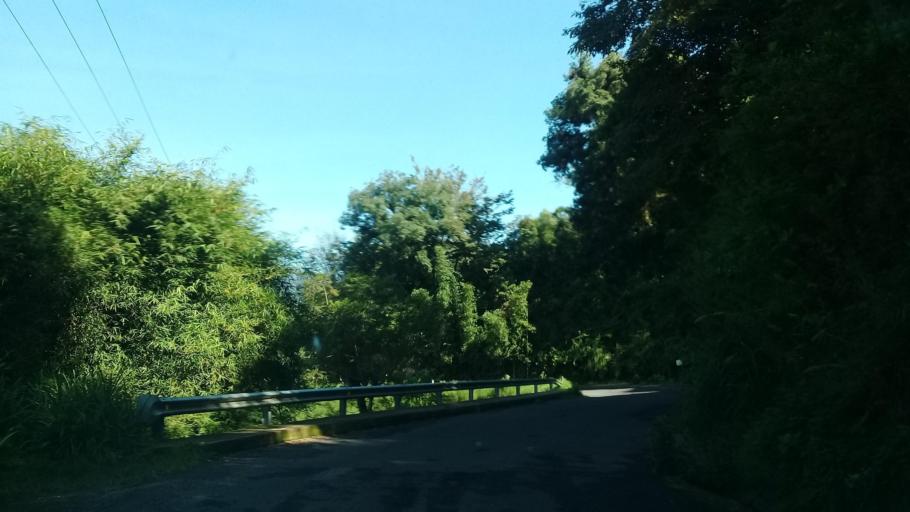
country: MX
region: Veracruz
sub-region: Tlalnelhuayocan
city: Guadalupe Victoria
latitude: 19.5280
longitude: -96.9486
